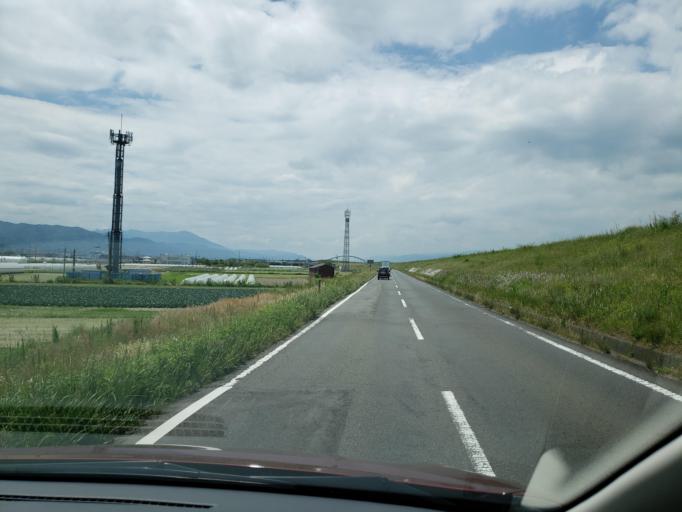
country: JP
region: Tokushima
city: Ishii
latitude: 34.0897
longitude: 134.4030
